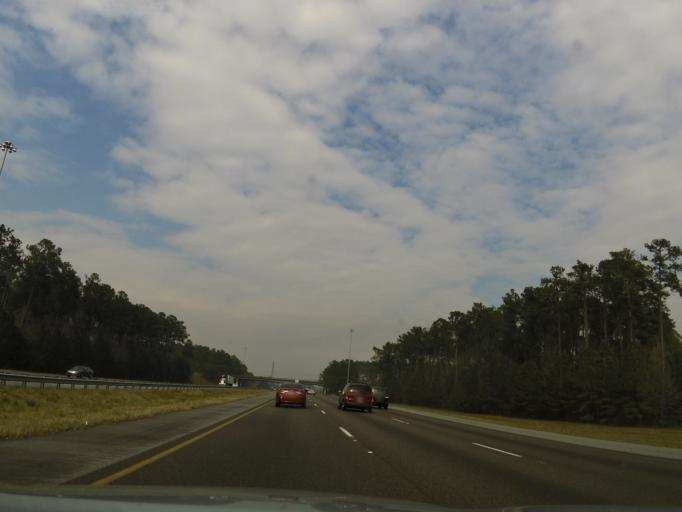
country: US
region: Georgia
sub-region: Liberty County
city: Midway
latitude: 31.7754
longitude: -81.3792
